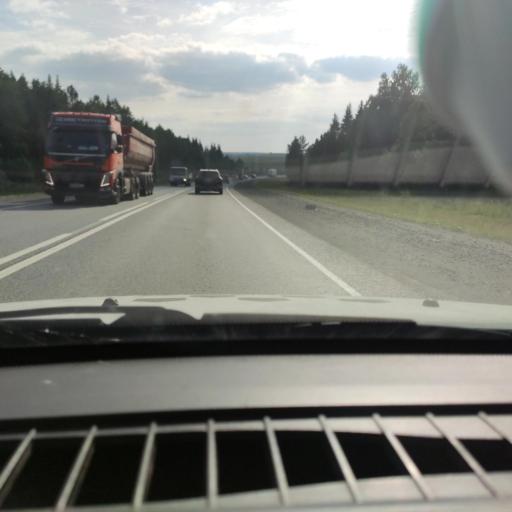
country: RU
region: Sverdlovsk
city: Druzhinino
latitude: 56.8116
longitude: 59.5552
